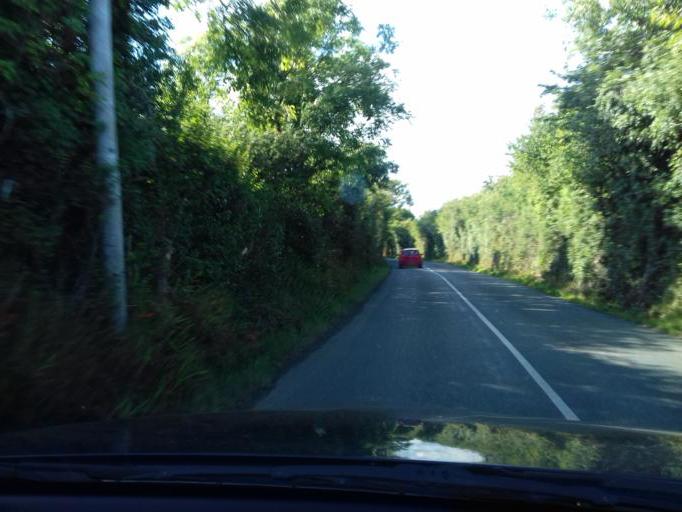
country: IE
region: Munster
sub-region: Waterford
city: Dunmore East
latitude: 52.2441
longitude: -6.8601
